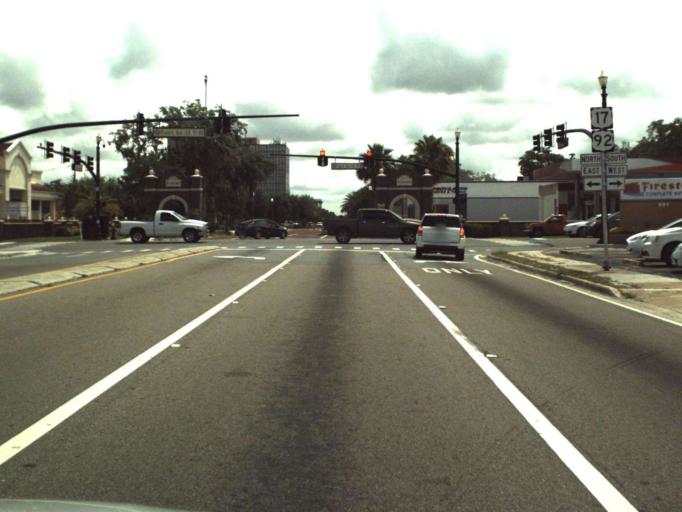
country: US
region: Florida
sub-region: Seminole County
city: Sanford
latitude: 28.8116
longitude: -81.2738
